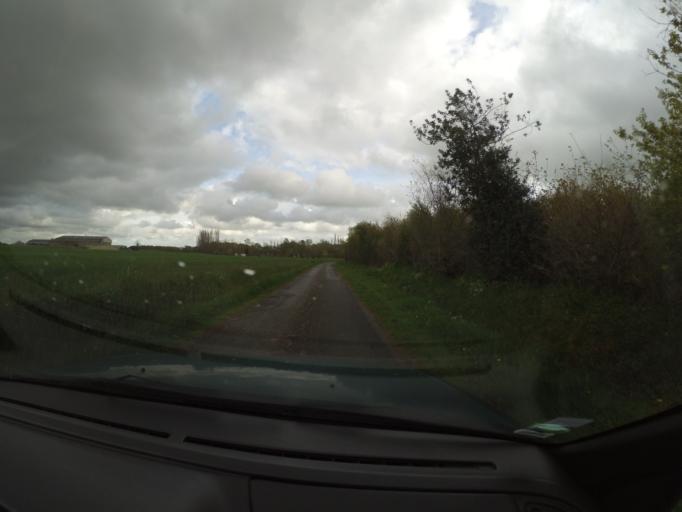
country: FR
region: Pays de la Loire
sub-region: Departement de la Loire-Atlantique
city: Remouille
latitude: 47.0716
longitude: -1.3613
